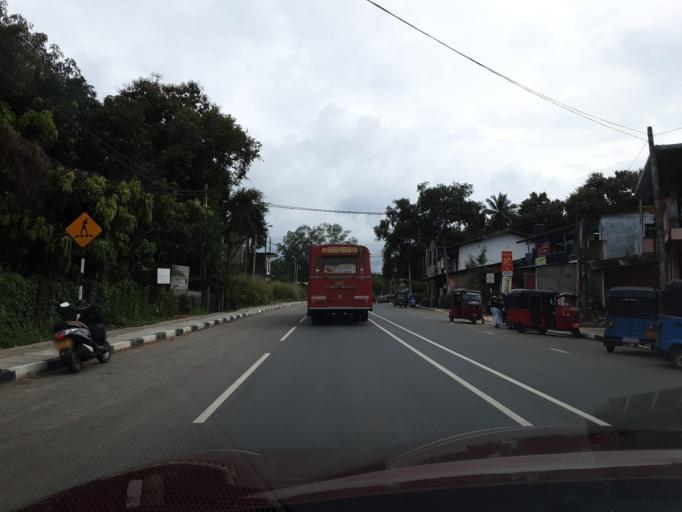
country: LK
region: Eastern Province
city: Ampara
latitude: 7.4027
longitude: 81.2434
